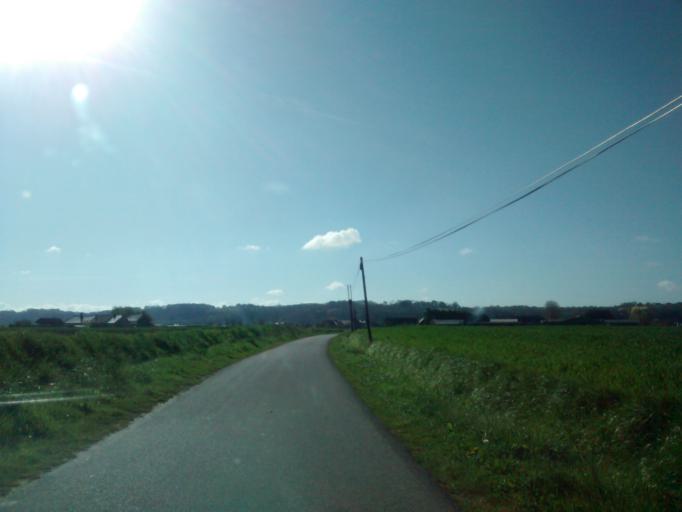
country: FR
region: Brittany
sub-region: Departement d'Ille-et-Vilaine
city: Saint-Broladre
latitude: 48.5973
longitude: -1.6668
